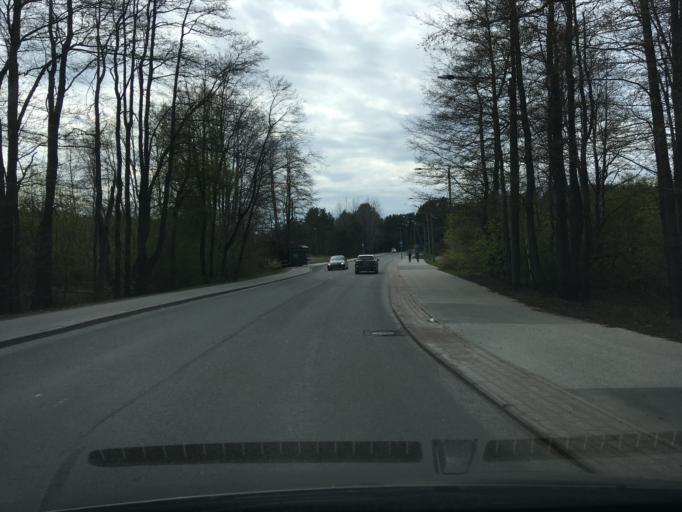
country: EE
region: Harju
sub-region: Tallinna linn
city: Kose
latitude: 59.4737
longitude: 24.9146
